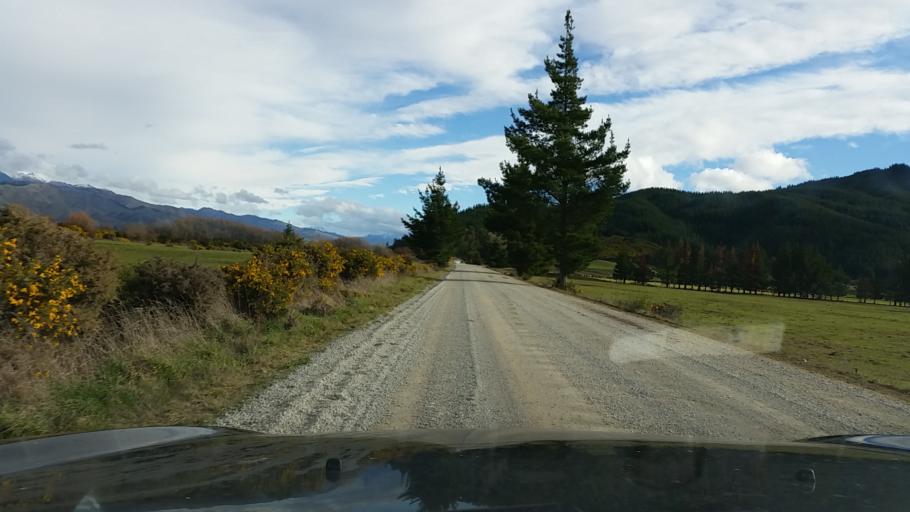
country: NZ
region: Nelson
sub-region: Nelson City
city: Nelson
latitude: -41.5680
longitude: 173.4561
